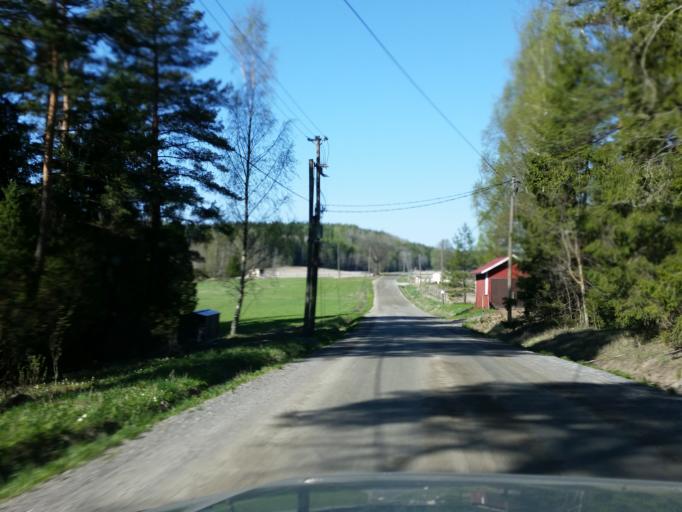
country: FI
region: Uusimaa
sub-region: Helsinki
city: Karjalohja
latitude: 60.1454
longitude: 23.8021
